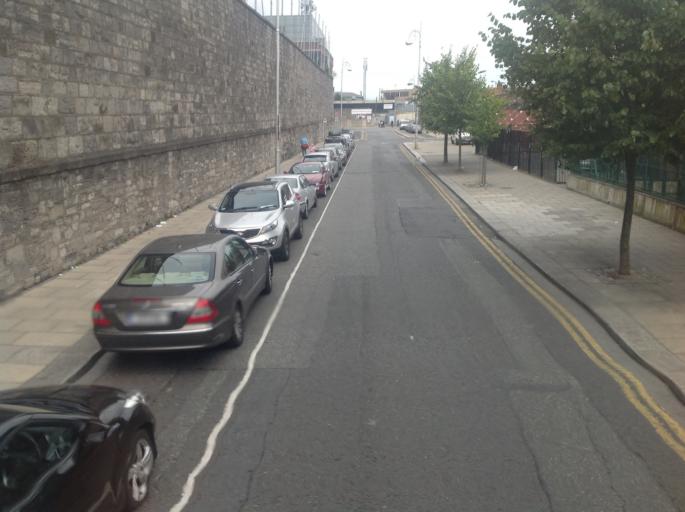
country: IE
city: Fairview
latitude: 53.3501
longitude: -6.2457
